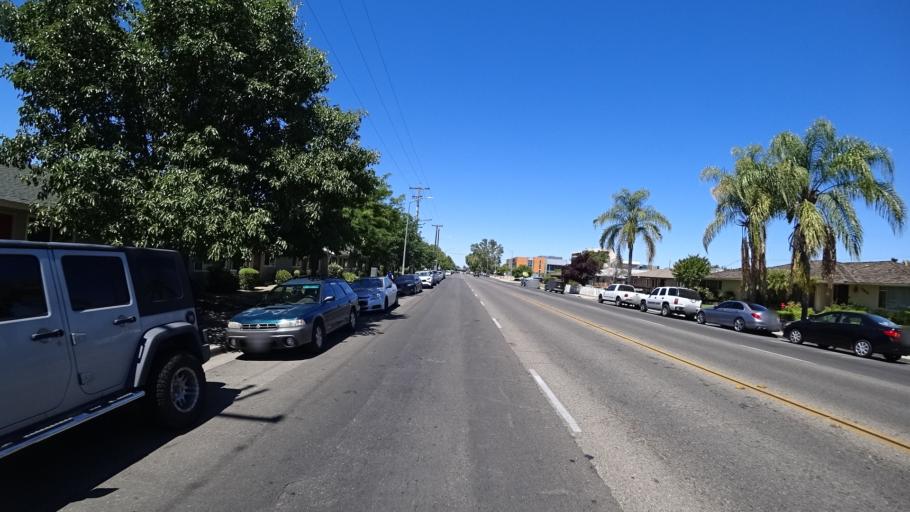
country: US
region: California
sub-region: Fresno County
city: Fresno
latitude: 36.7722
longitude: -119.7759
